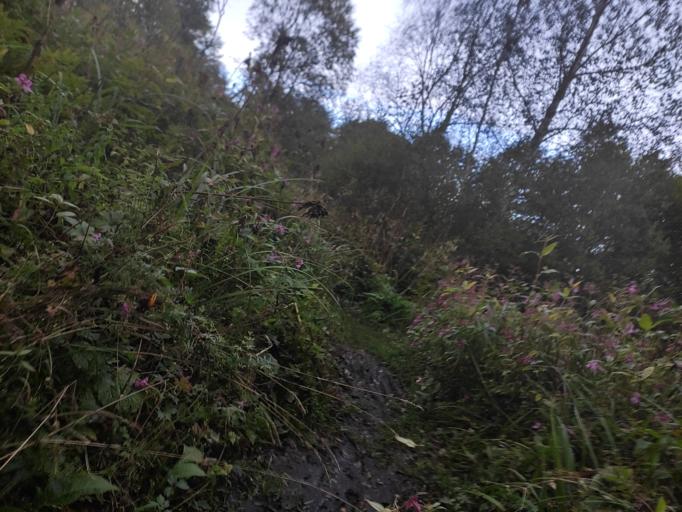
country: RU
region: Moskovskaya
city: Izmaylovo
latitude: 55.7802
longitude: 37.7888
